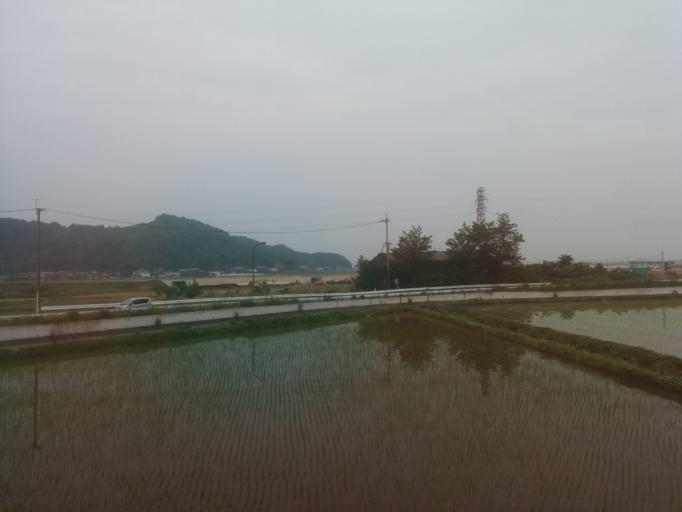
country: JP
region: Shiga Prefecture
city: Omihachiman
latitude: 35.1570
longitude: 136.1494
